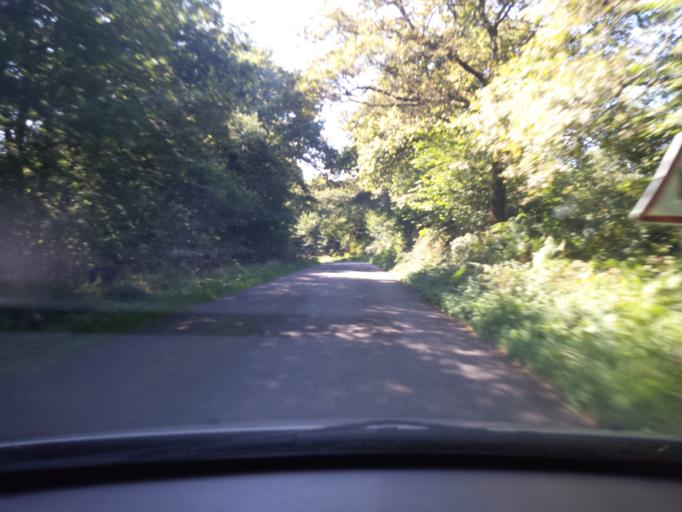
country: FR
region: Brittany
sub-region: Departement des Cotes-d'Armor
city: Plounevez-Quintin
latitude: 48.3396
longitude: -3.2616
